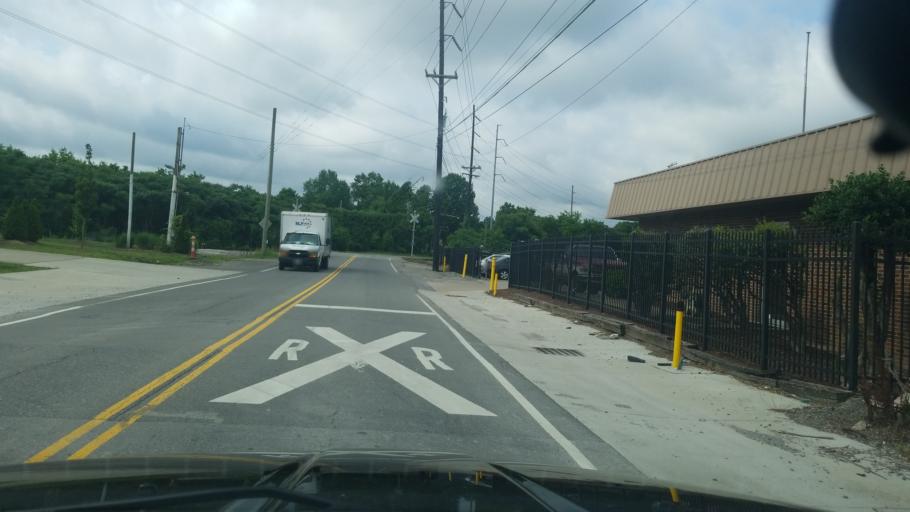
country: US
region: Tennessee
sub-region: Davidson County
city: Oak Hill
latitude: 36.0910
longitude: -86.7501
